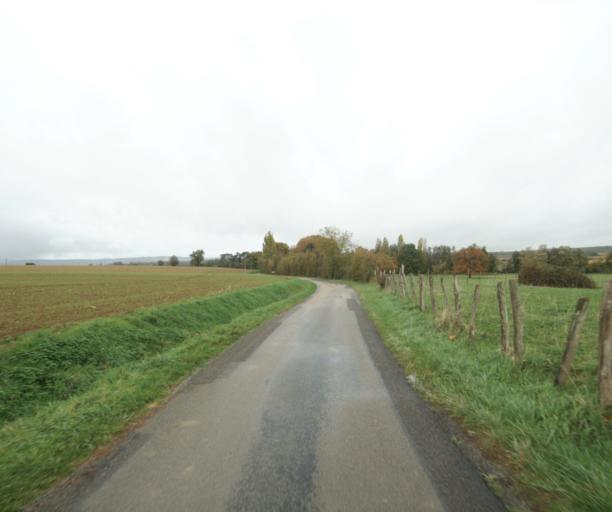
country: FR
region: Rhone-Alpes
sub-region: Departement de l'Ain
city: Pont-de-Vaux
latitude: 46.4789
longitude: 4.8728
